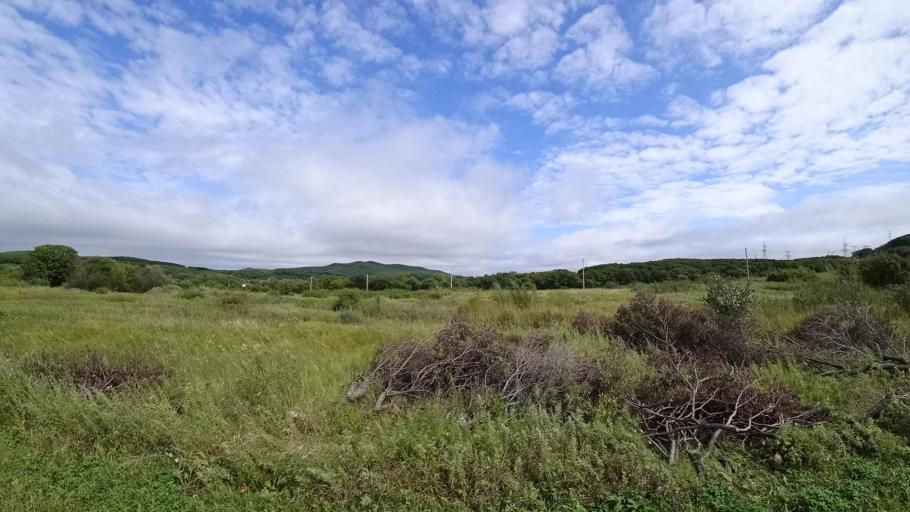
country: RU
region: Primorskiy
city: Lyalichi
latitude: 44.1313
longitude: 132.3881
